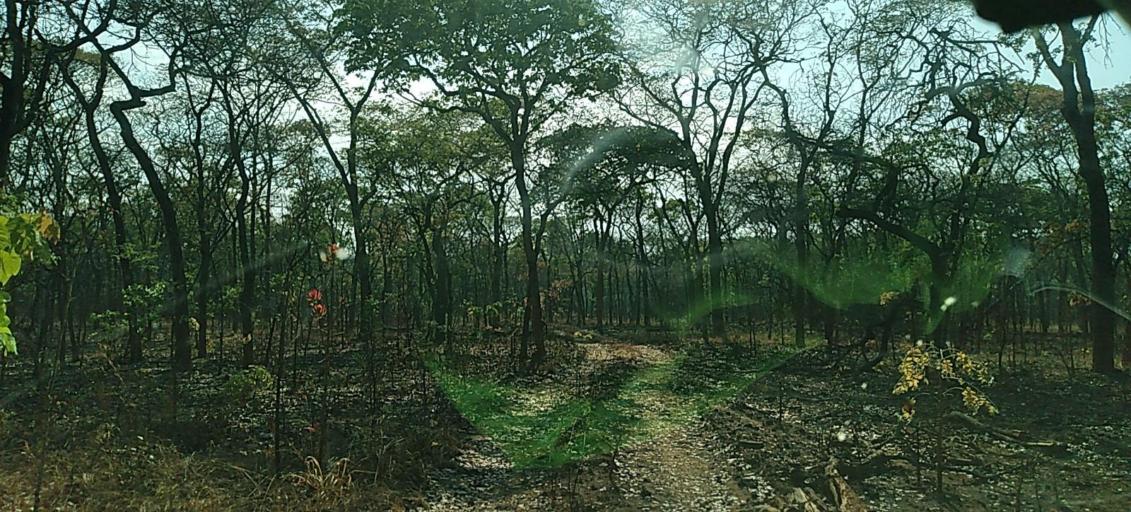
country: ZM
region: North-Western
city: Kalengwa
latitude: -13.2286
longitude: 25.0811
